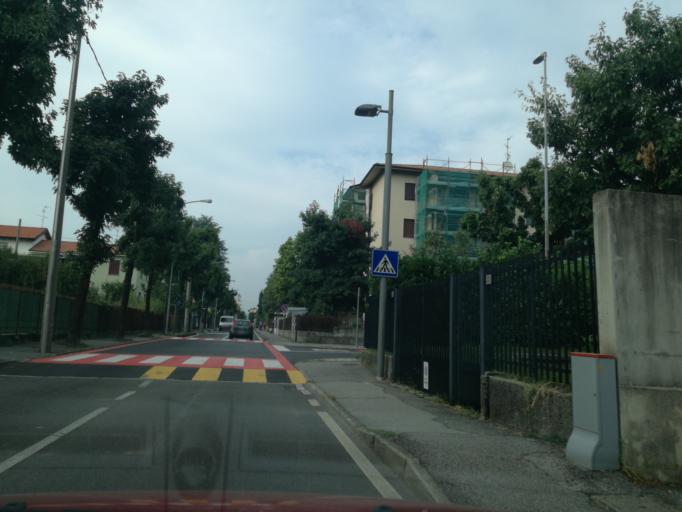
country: IT
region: Lombardy
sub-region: Provincia di Monza e Brianza
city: Vimercate
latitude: 45.6244
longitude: 9.3697
